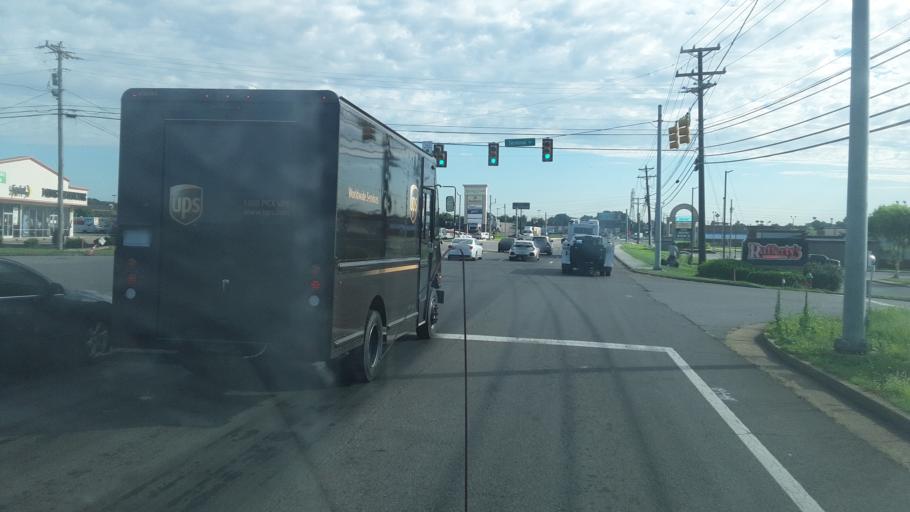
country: US
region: Tennessee
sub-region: Montgomery County
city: Clarksville
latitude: 36.5877
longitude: -87.2938
